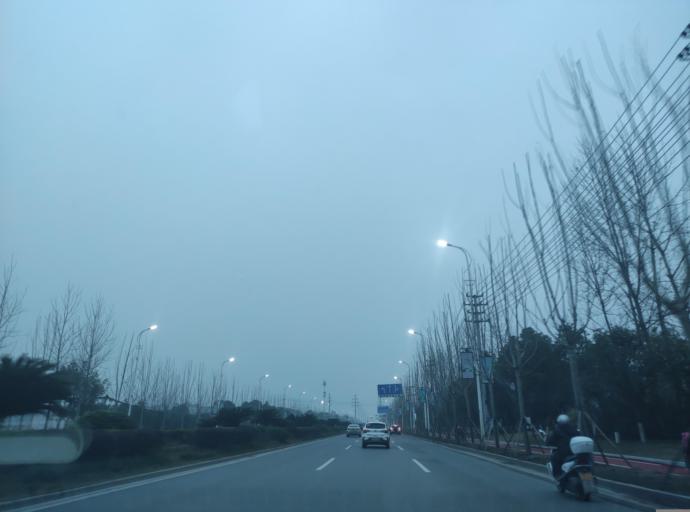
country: CN
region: Jiangxi Sheng
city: Pingxiang
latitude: 27.6673
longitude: 113.8741
